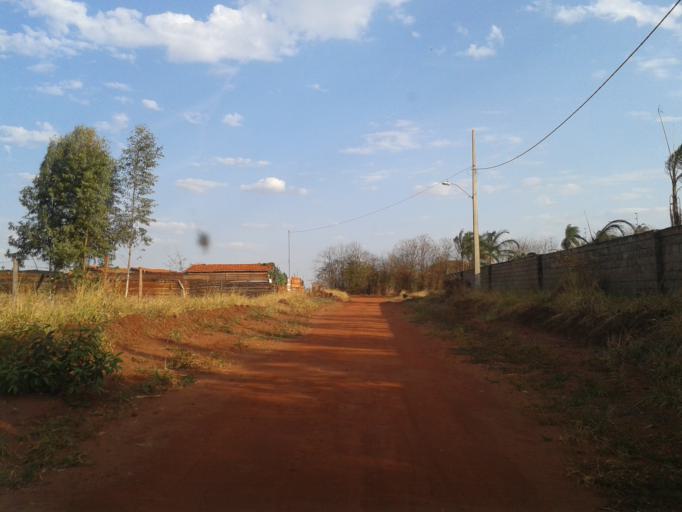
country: BR
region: Minas Gerais
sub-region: Ituiutaba
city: Ituiutaba
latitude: -18.9959
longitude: -49.4350
